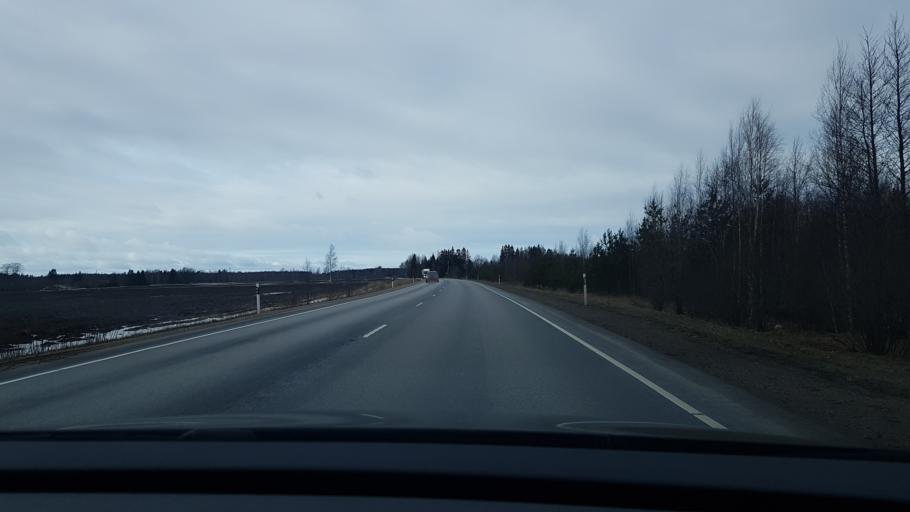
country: EE
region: Paernumaa
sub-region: Paikuse vald
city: Paikuse
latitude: 58.2608
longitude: 24.6683
